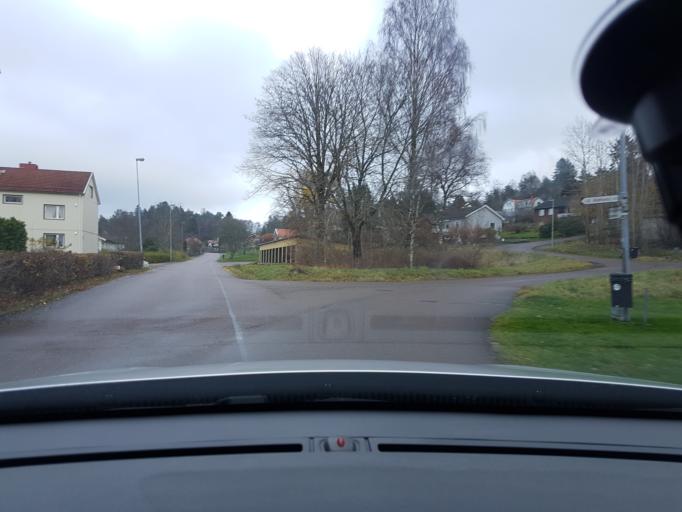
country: SE
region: Vaestra Goetaland
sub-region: Ale Kommun
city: Alafors
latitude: 57.9178
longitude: 12.0718
